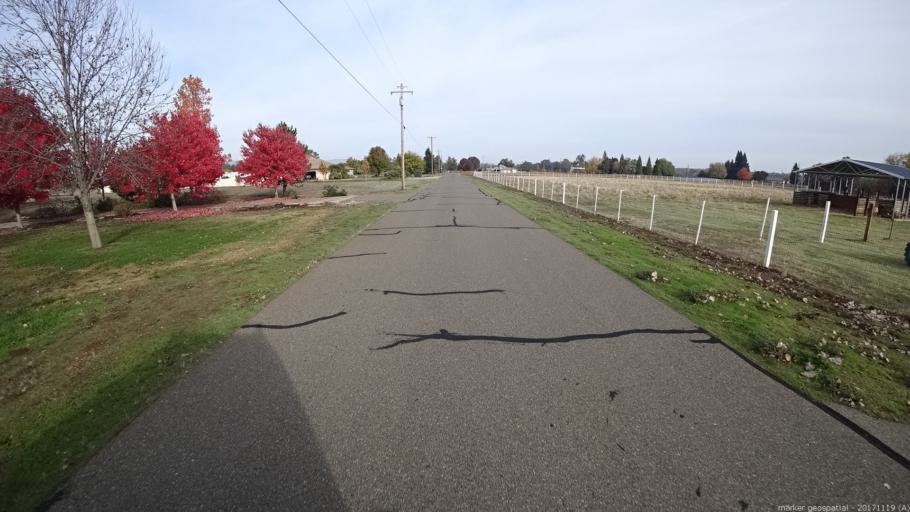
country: US
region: California
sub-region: Shasta County
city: Anderson
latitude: 40.5092
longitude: -122.3291
